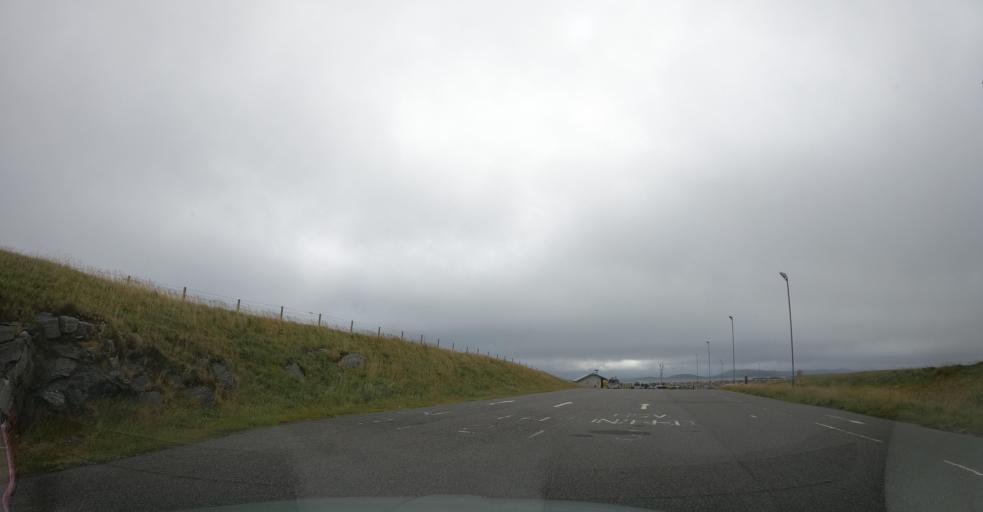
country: GB
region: Scotland
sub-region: Eilean Siar
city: Isle of North Uist
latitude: 57.7036
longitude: -7.1819
